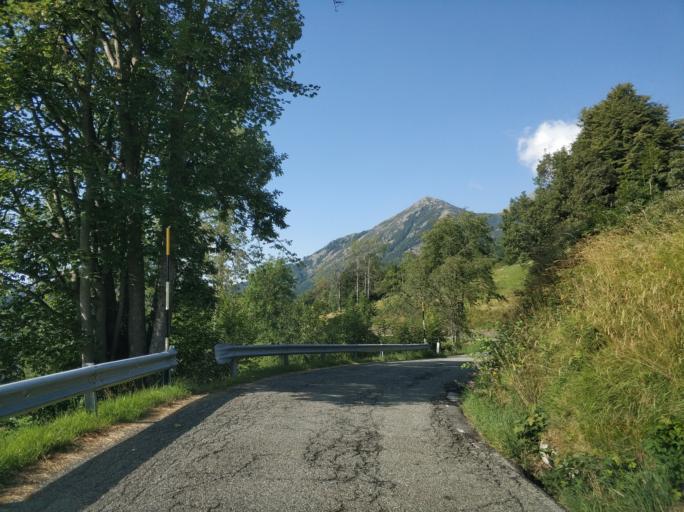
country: IT
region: Piedmont
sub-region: Provincia di Torino
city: Viu
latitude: 45.2044
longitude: 7.3772
